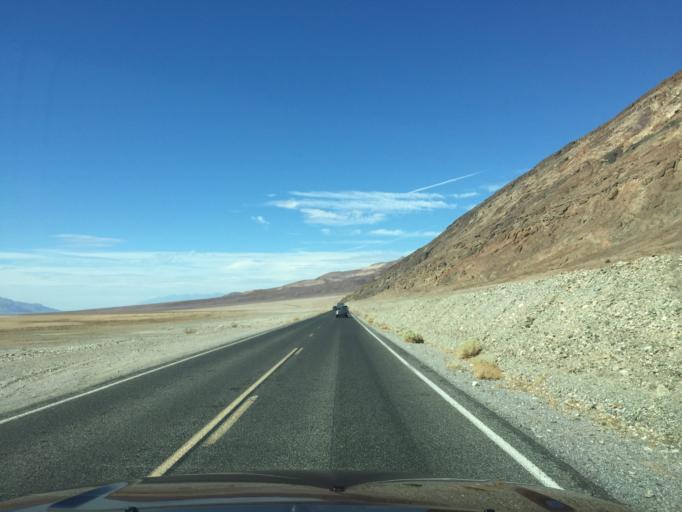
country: US
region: Nevada
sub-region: Nye County
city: Beatty
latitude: 36.2422
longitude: -116.7720
